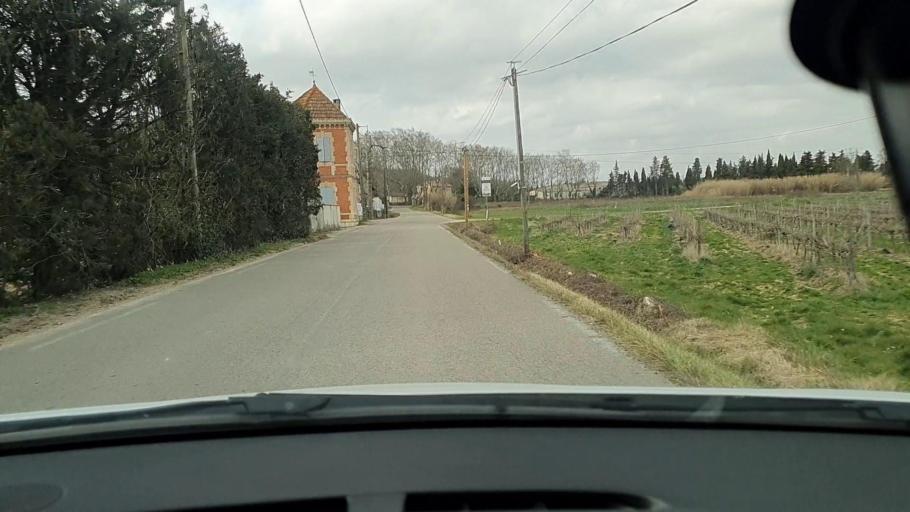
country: FR
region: Languedoc-Roussillon
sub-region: Departement du Gard
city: Montfrin
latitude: 43.8706
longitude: 4.5791
